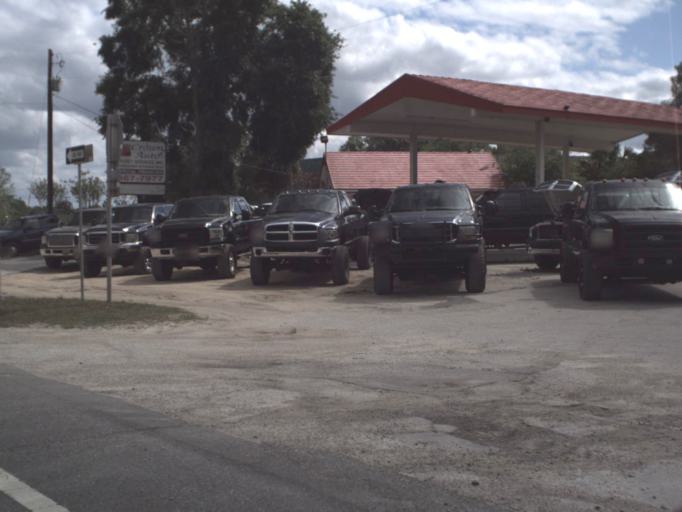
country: US
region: Florida
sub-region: Marion County
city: Ocala
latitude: 29.2118
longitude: -82.1436
